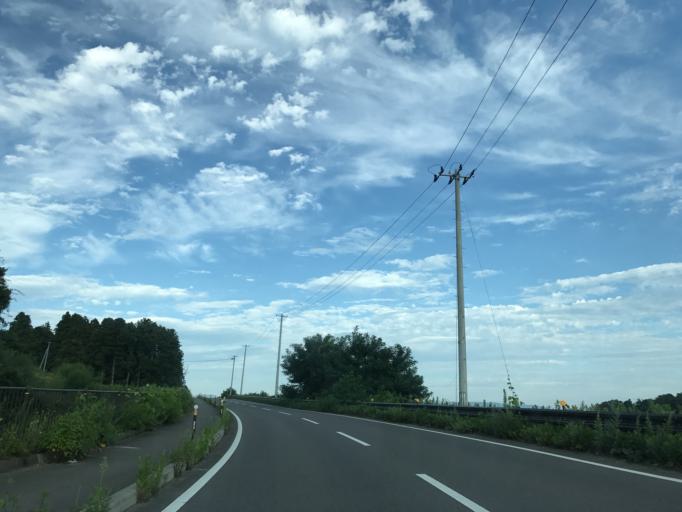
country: JP
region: Fukushima
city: Sukagawa
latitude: 37.3292
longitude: 140.3443
